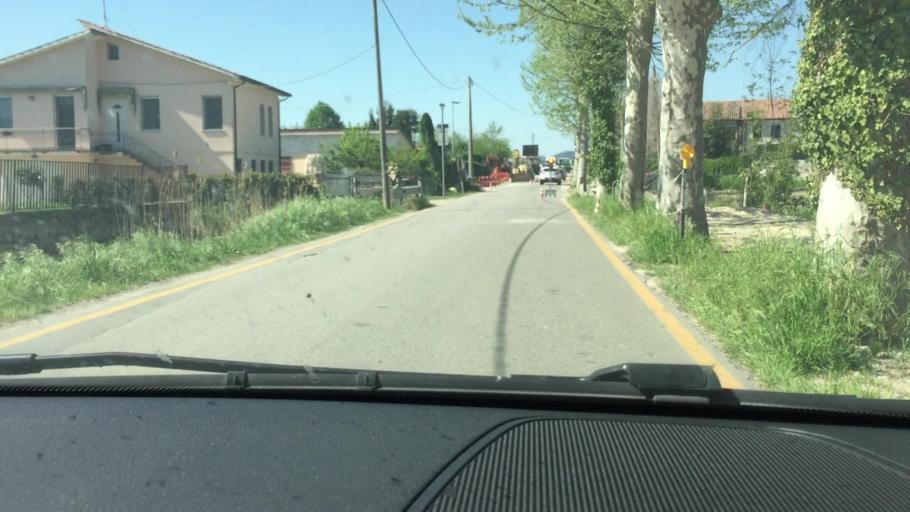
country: IT
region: Veneto
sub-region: Provincia di Padova
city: Pernumia
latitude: 45.2637
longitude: 11.7860
